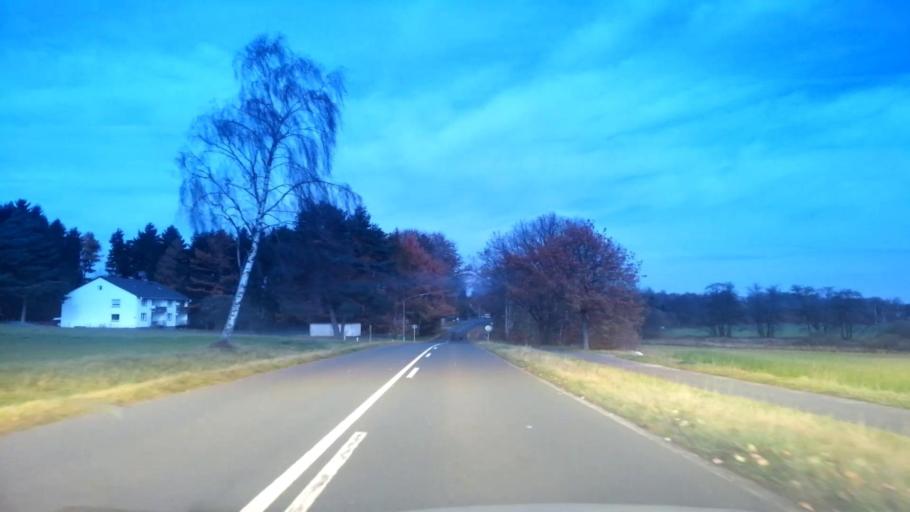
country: DE
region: Bavaria
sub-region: Upper Palatinate
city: Waldsassen
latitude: 50.0199
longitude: 12.3220
